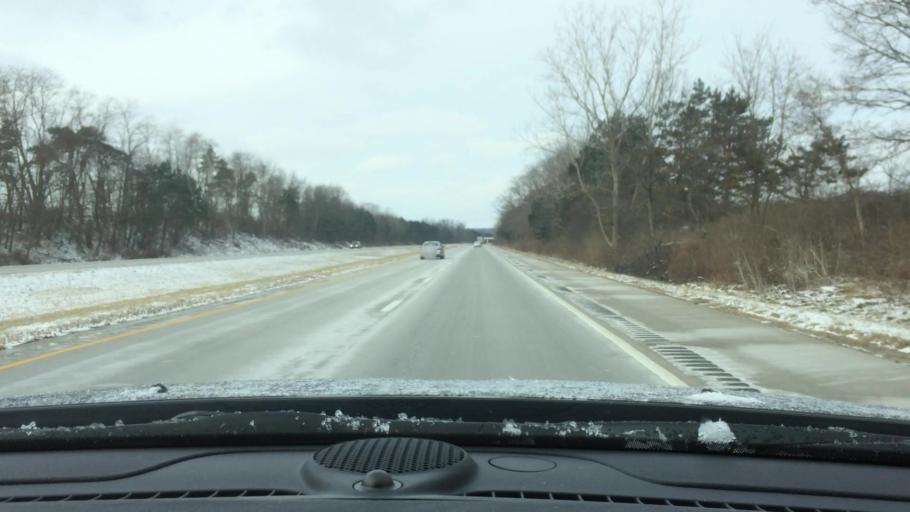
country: US
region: Ohio
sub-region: Wayne County
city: Dalton
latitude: 40.7925
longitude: -81.6355
